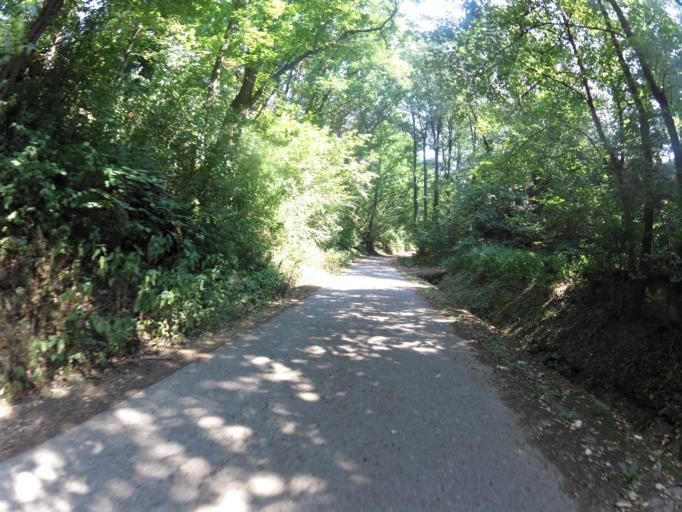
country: DE
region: Bavaria
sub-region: Regierungsbezirk Unterfranken
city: Ochsenfurt
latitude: 49.6547
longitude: 10.0582
